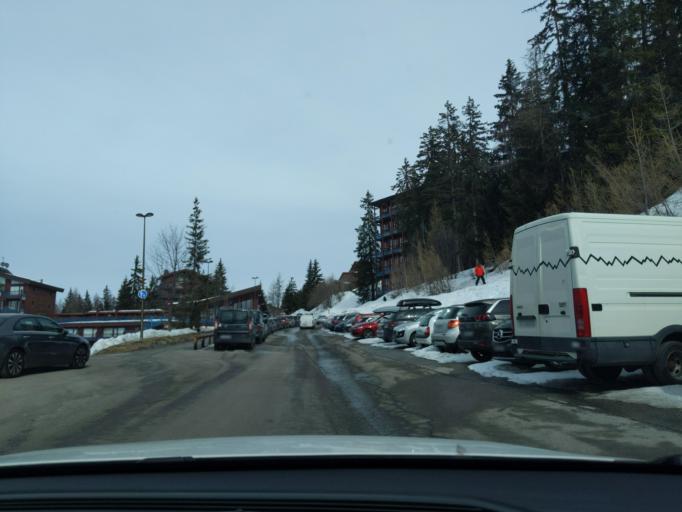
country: FR
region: Rhone-Alpes
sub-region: Departement de la Savoie
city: Bourg-Saint-Maurice
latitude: 45.5695
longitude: 6.7756
